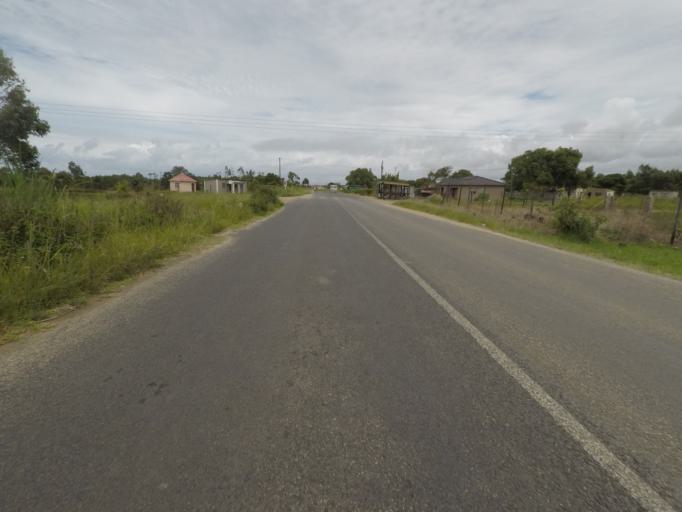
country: ZA
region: KwaZulu-Natal
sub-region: uThungulu District Municipality
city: eSikhawini
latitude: -28.9061
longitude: 31.8836
